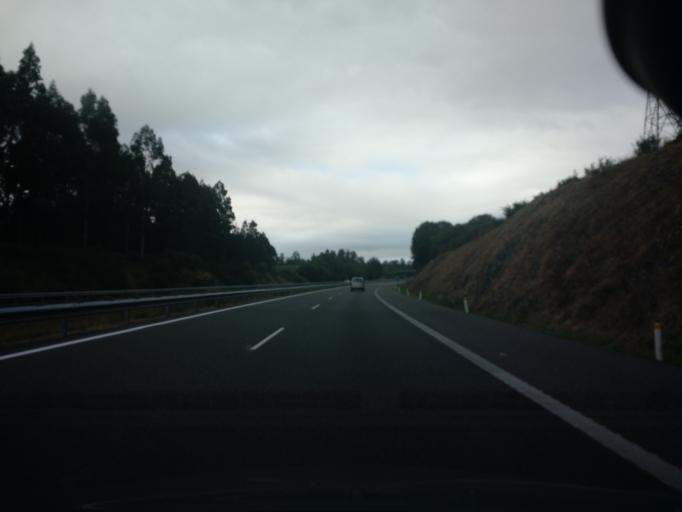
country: ES
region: Galicia
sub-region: Provincia da Coruna
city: Abegondo
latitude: 43.2171
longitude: -8.2757
